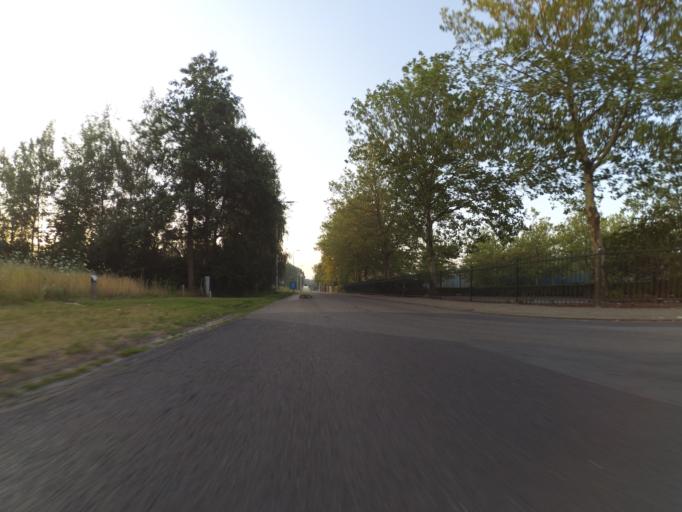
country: NL
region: Overijssel
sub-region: Gemeente Tubbergen
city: Tubbergen
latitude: 52.4054
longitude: 6.7884
